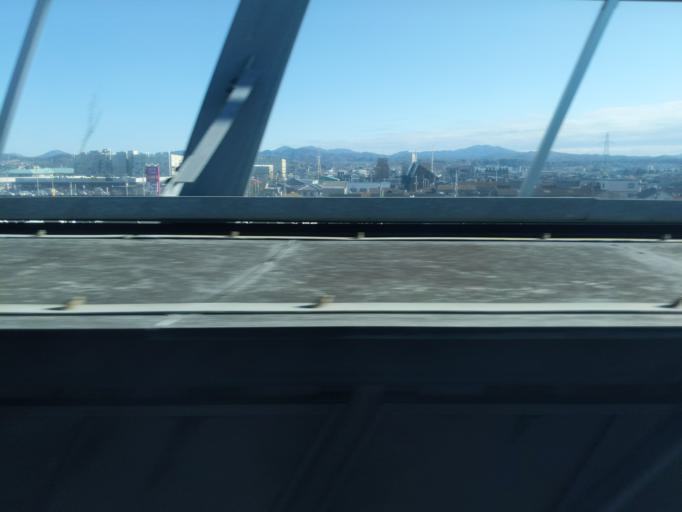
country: JP
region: Fukushima
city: Koriyama
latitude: 37.3888
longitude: 140.3863
